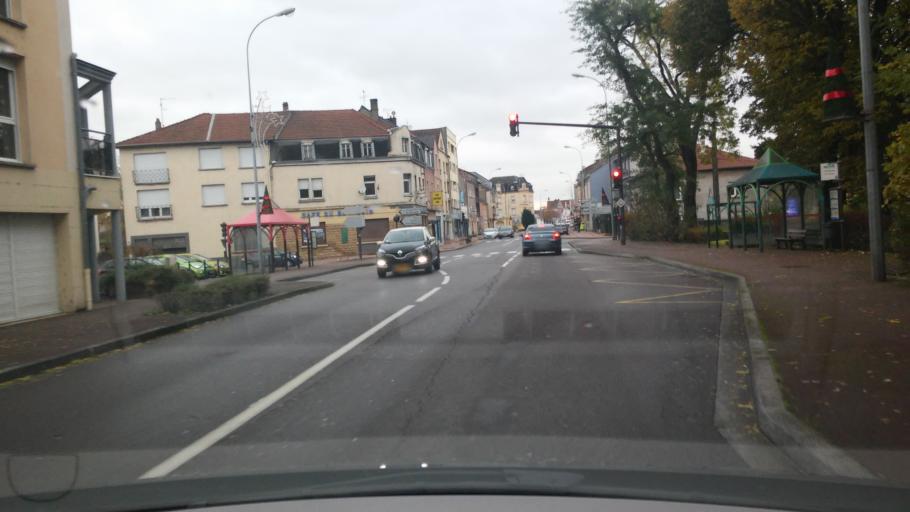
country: FR
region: Lorraine
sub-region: Departement de la Moselle
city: Hagondange
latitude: 49.2482
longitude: 6.1702
